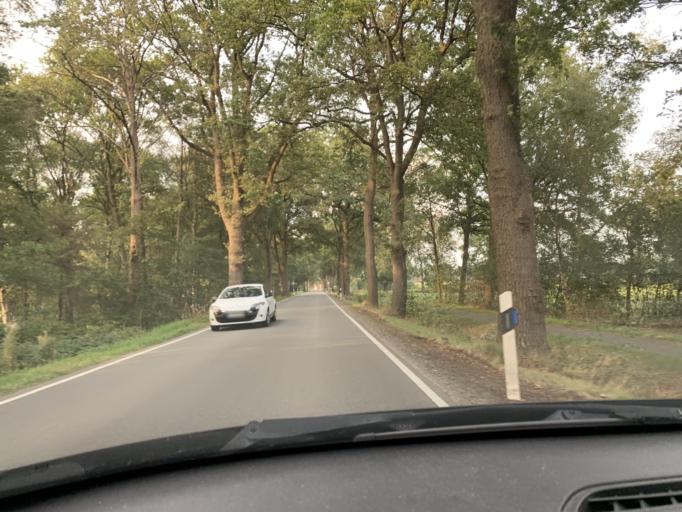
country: DE
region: Lower Saxony
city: Apen
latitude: 53.2057
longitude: 7.7943
